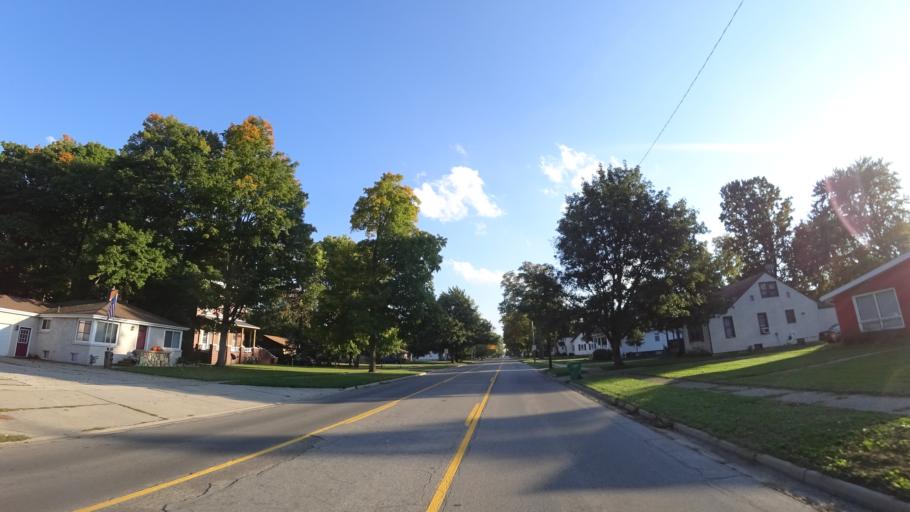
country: US
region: Michigan
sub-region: Saint Joseph County
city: Three Rivers
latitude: 41.9569
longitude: -85.6348
